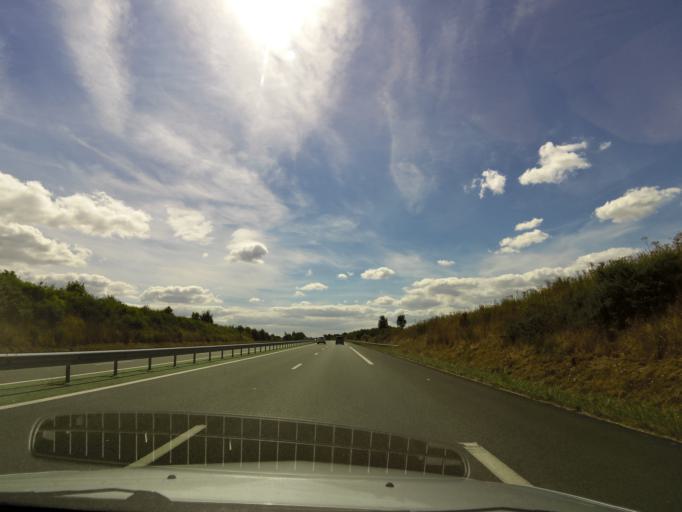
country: FR
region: Pays de la Loire
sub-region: Departement de la Vendee
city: Les Essarts
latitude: 46.7894
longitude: -1.2441
